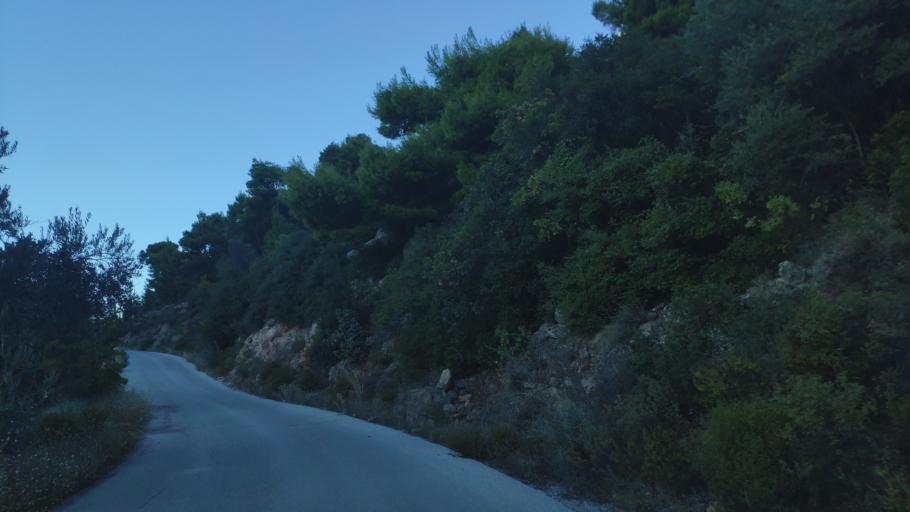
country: GR
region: Attica
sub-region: Nomos Piraios
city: Megalochori
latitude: 37.6176
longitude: 23.3367
